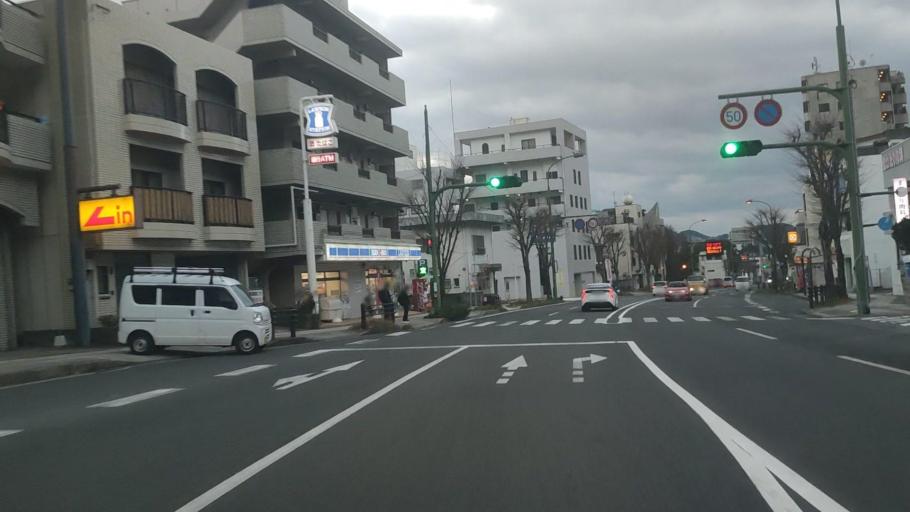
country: JP
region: Nagasaki
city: Nagasaki-shi
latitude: 32.7624
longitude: 129.8888
